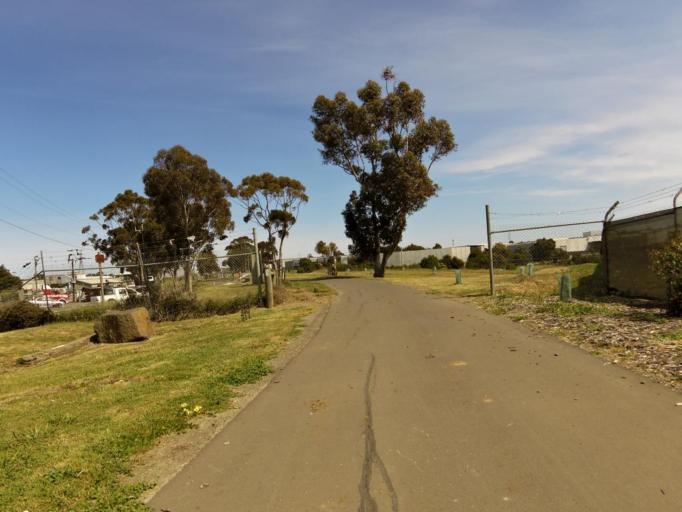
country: AU
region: Victoria
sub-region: Brimbank
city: Brooklyn
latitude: -37.8193
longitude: 144.8278
